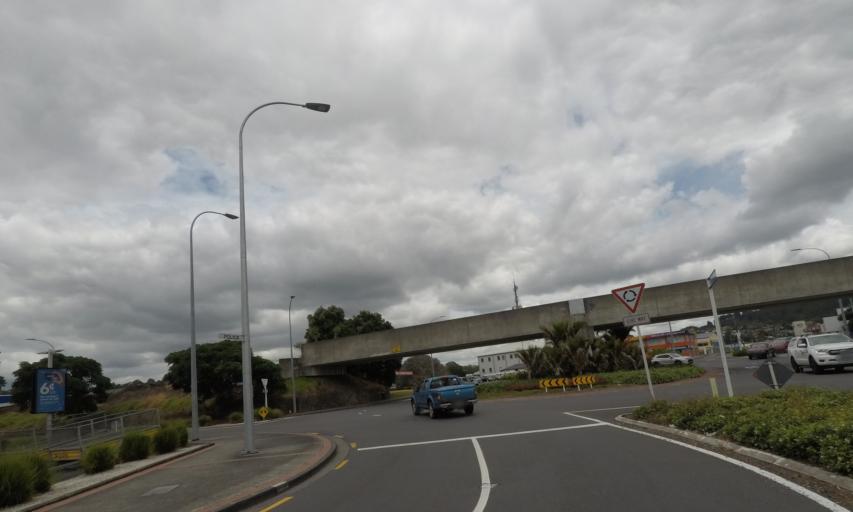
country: NZ
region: Northland
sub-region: Whangarei
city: Whangarei
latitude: -35.7274
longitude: 174.3197
